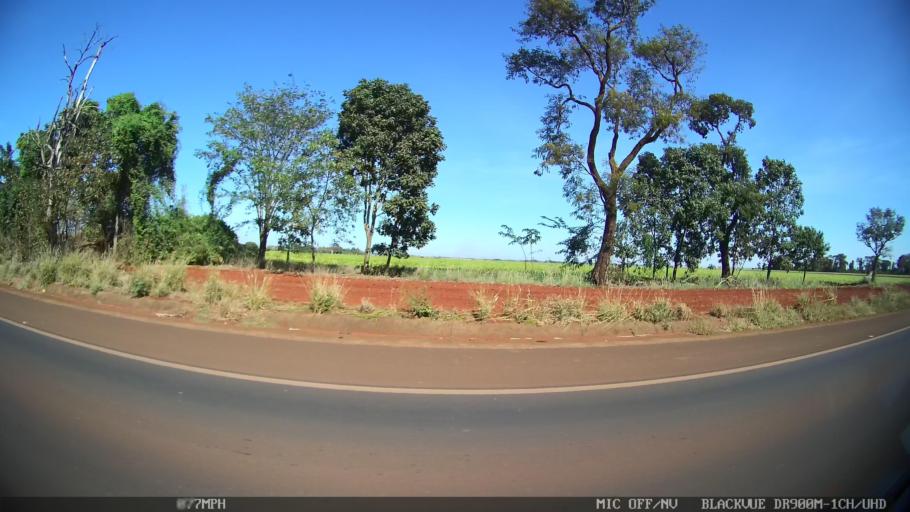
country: BR
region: Sao Paulo
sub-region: Guaira
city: Guaira
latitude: -20.4447
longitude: -48.3758
